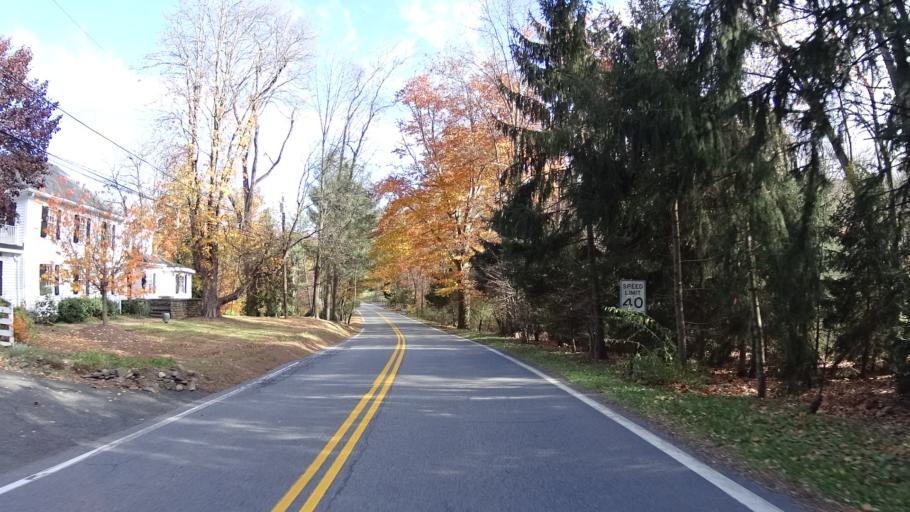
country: US
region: New Jersey
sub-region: Somerset County
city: Bernardsville
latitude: 40.7551
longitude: -74.5385
